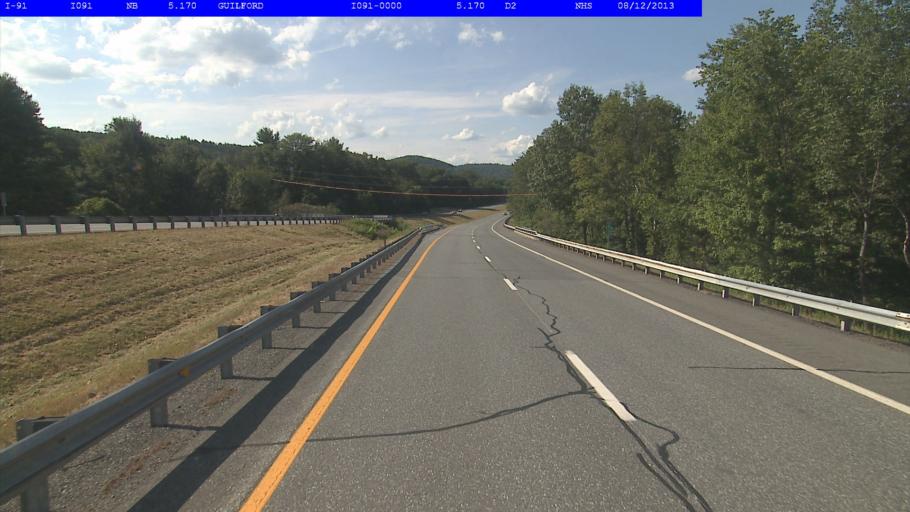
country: US
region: Vermont
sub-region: Windham County
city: Brattleboro
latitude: 42.8040
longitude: -72.5641
